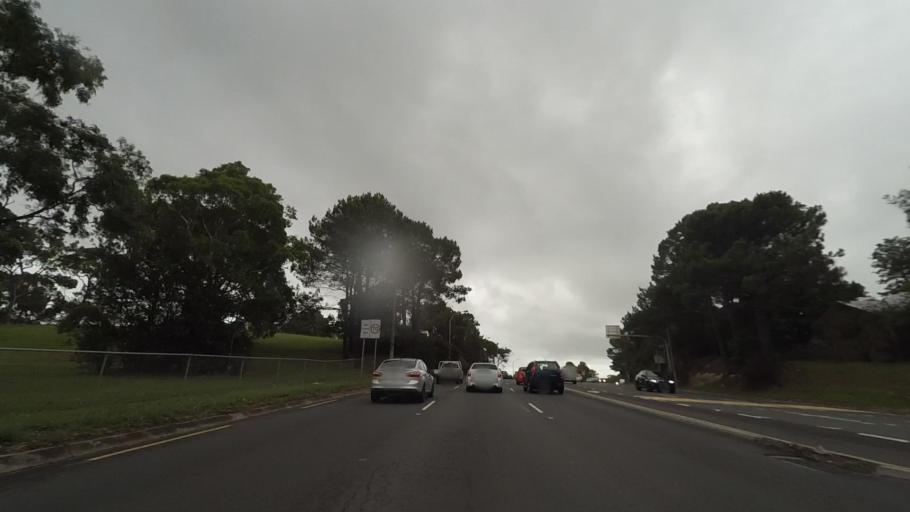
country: AU
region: New South Wales
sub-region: Sutherland Shire
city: Caringbah
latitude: -34.0183
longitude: 151.1219
